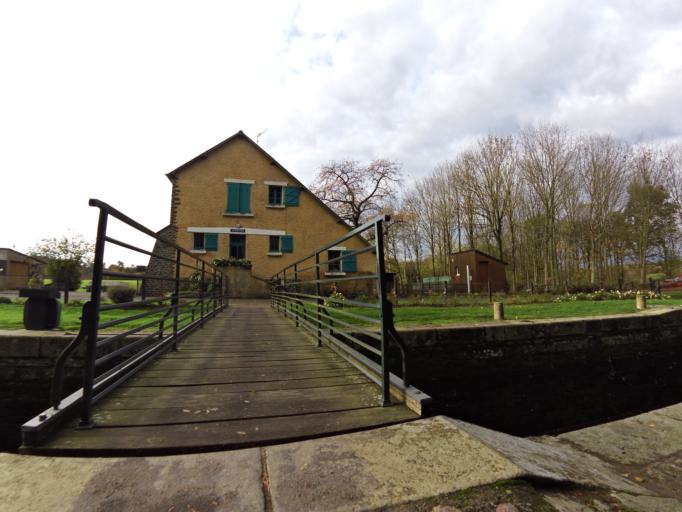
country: FR
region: Brittany
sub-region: Departement d'Ille-et-Vilaine
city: Bourg-des-Comptes
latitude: 47.9266
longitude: -1.7492
